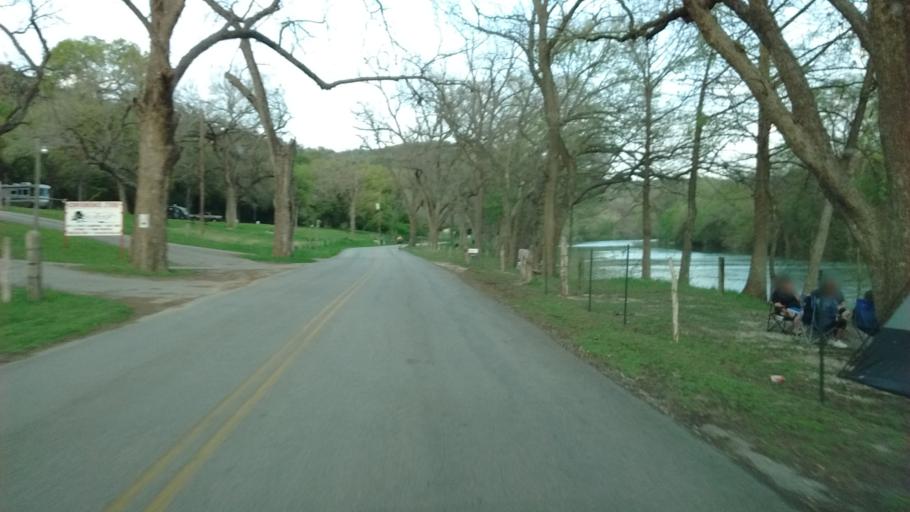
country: US
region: Texas
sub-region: Comal County
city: New Braunfels
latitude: 29.7662
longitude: -98.1498
